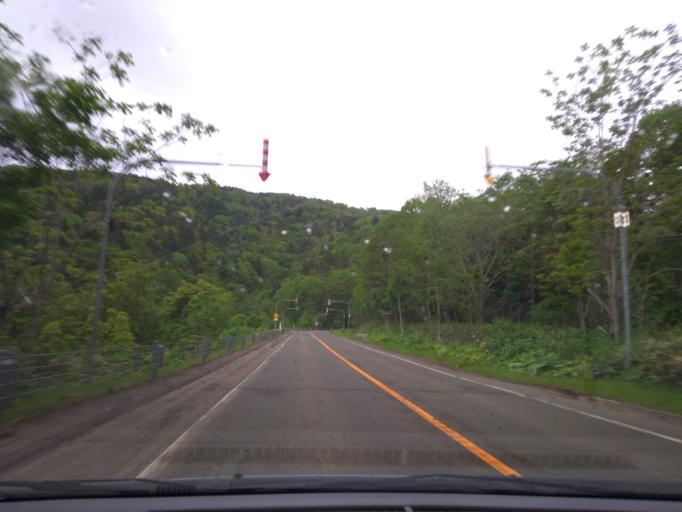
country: JP
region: Hokkaido
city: Shimo-furano
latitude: 43.0932
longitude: 142.4041
